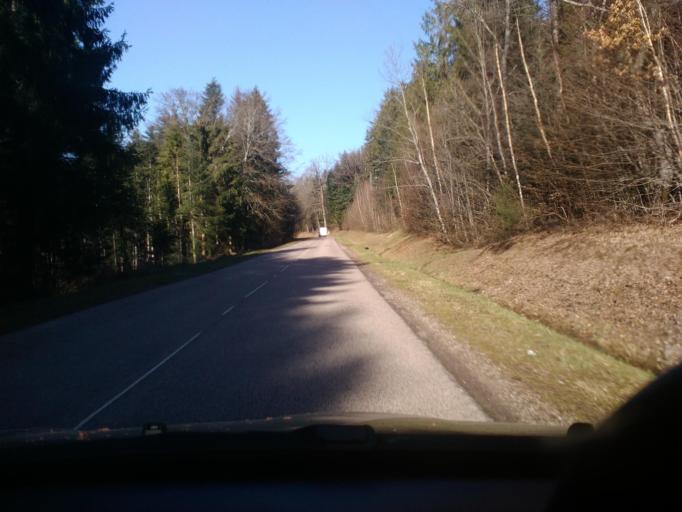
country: FR
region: Lorraine
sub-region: Departement des Vosges
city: Moyenmoutier
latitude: 48.3498
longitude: 6.9469
